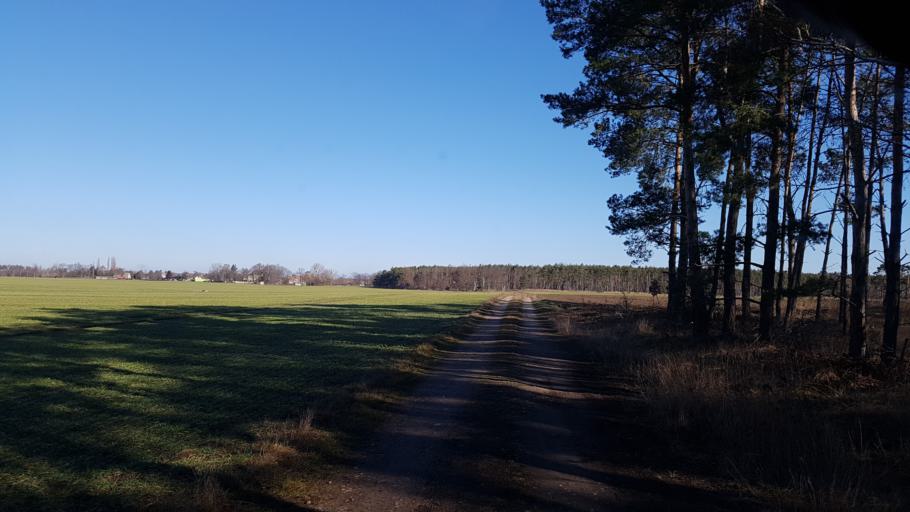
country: DE
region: Brandenburg
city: Falkenberg
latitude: 51.5289
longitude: 13.2273
